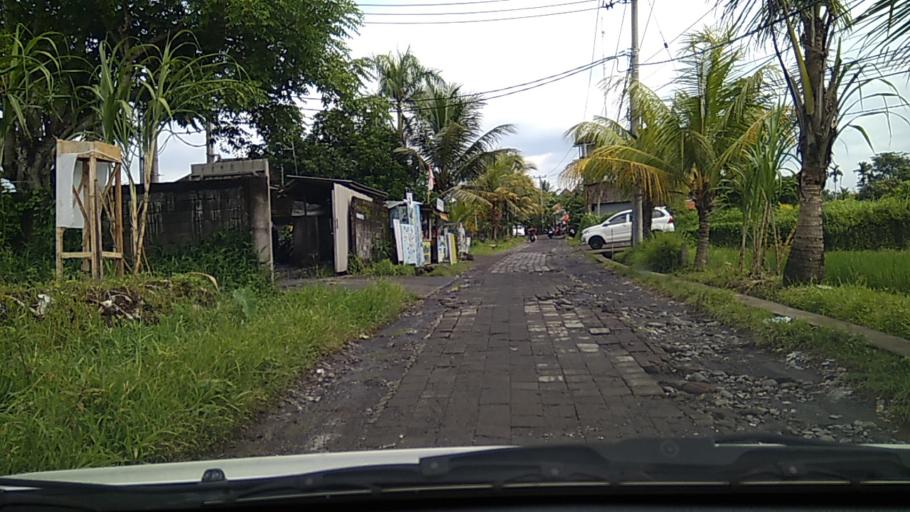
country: ID
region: Bali
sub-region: Kabupaten Gianyar
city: Ubud
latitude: -8.5138
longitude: 115.2582
